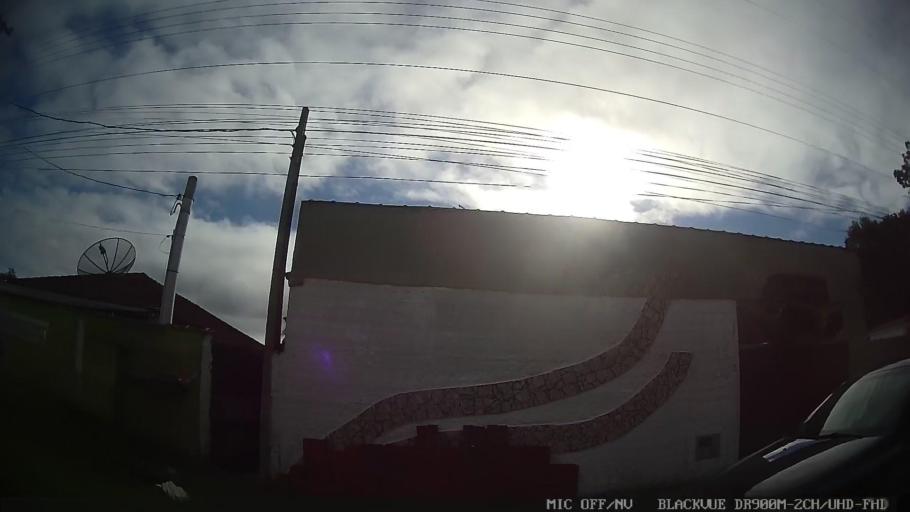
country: BR
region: Sao Paulo
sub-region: Peruibe
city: Peruibe
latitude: -24.2301
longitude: -46.9172
